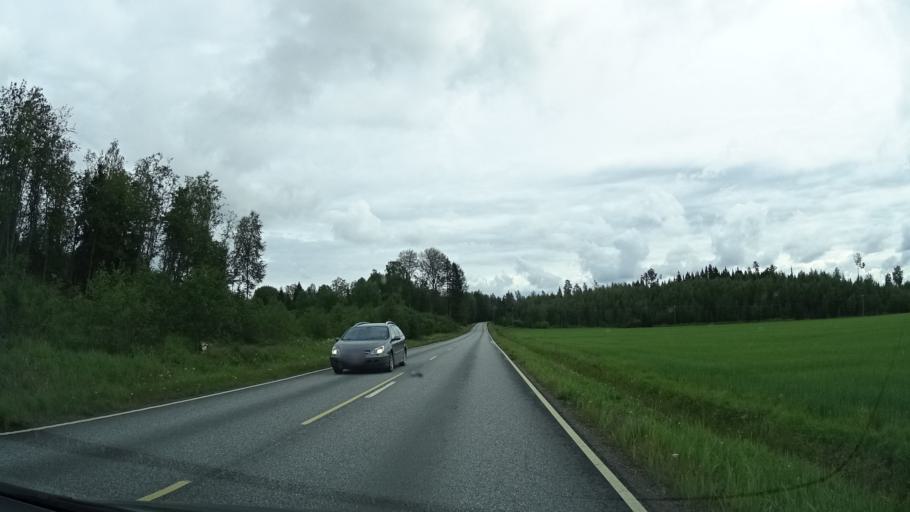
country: FI
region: Pirkanmaa
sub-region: Etelae-Pirkanmaa
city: Urjala
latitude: 61.0921
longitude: 23.3863
